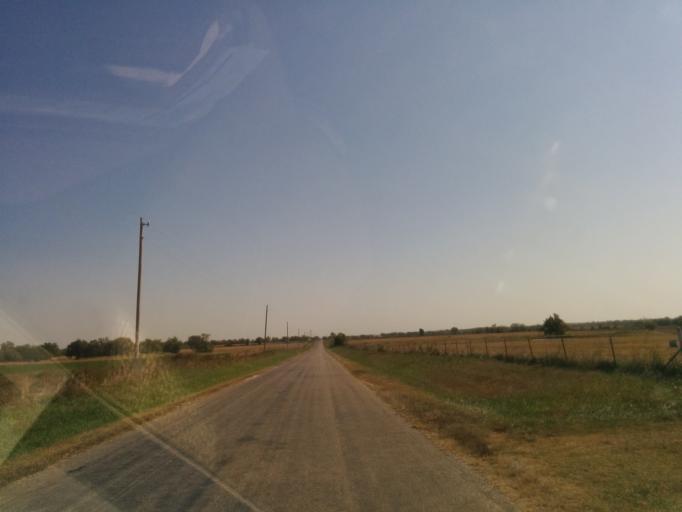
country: US
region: Oklahoma
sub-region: Okmulgee County
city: Beggs
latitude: 35.7991
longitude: -96.0843
